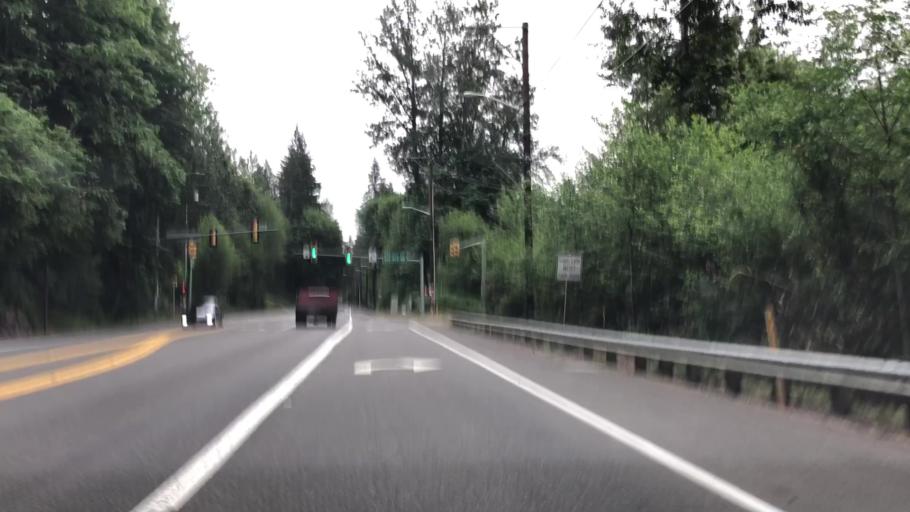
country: US
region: Washington
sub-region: King County
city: Cottage Lake
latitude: 47.7540
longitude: -122.0534
